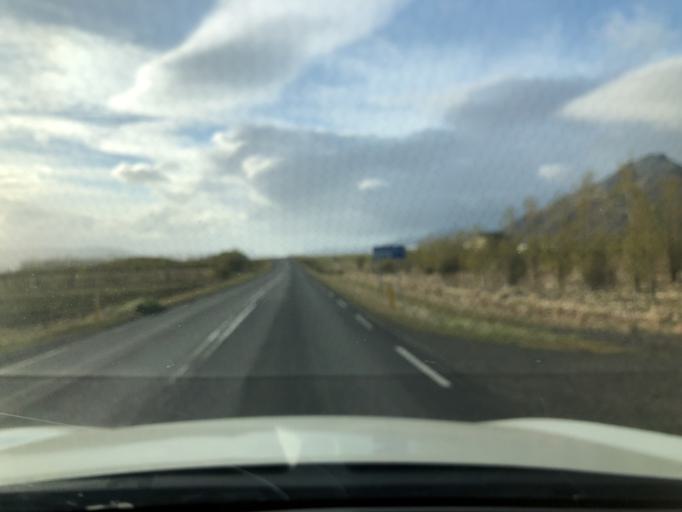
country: IS
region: East
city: Hoefn
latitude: 64.3024
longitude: -15.2045
